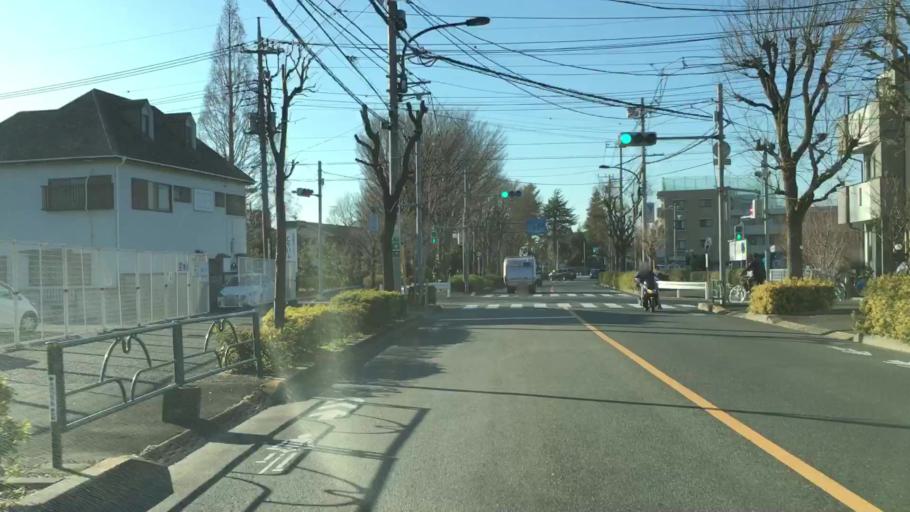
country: JP
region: Tokyo
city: Musashino
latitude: 35.7085
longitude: 139.5543
